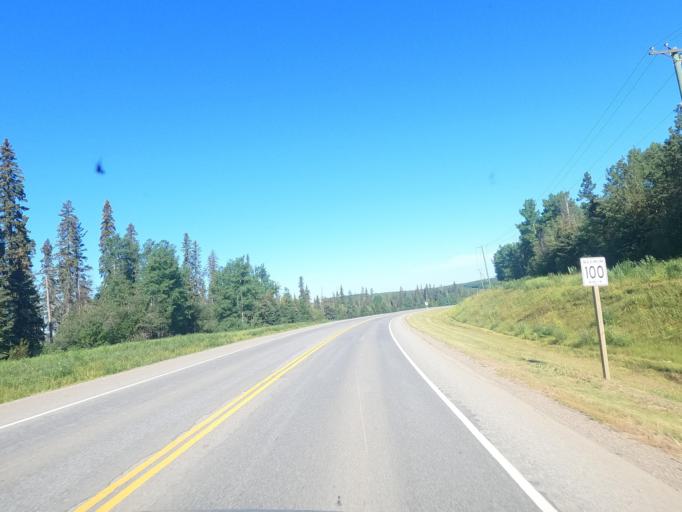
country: CA
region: British Columbia
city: Fort St. John
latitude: 56.5960
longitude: -121.4617
